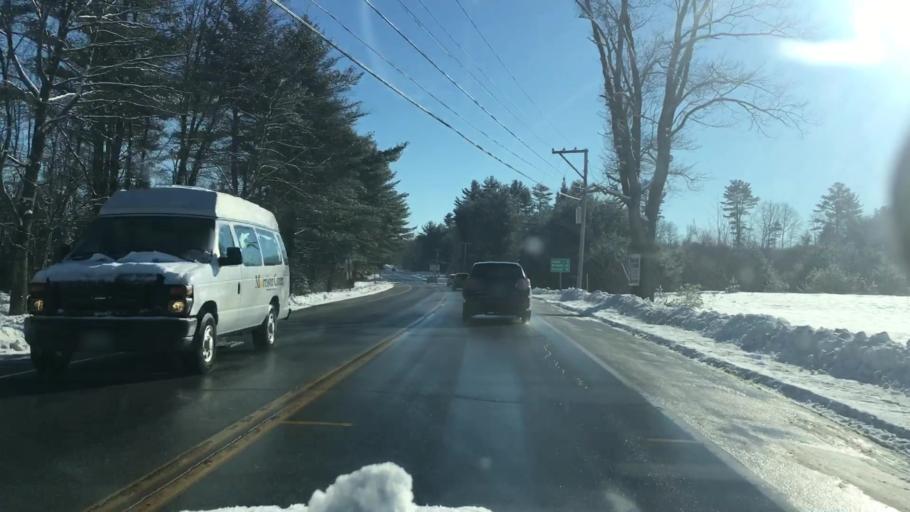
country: US
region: Maine
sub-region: Cumberland County
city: Bridgton
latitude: 44.0314
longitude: -70.6959
